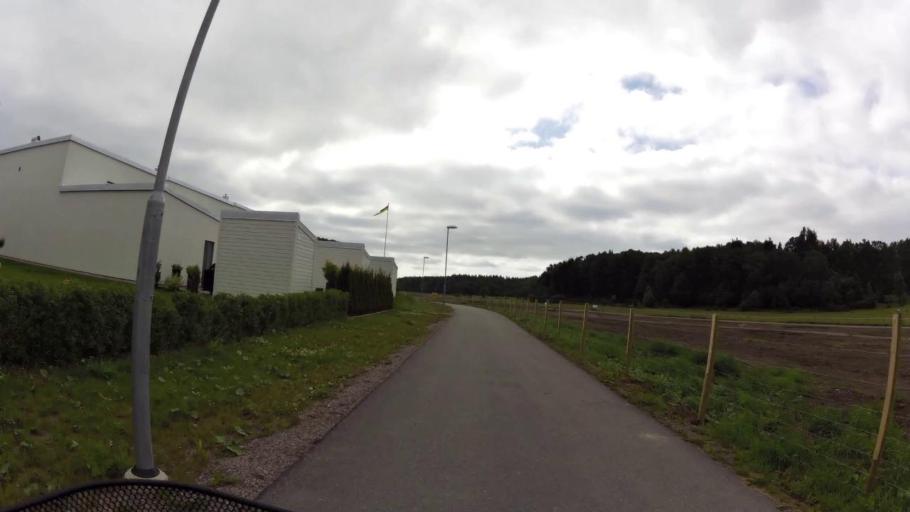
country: SE
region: OEstergoetland
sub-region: Linkopings Kommun
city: Sturefors
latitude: 58.3631
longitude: 15.6785
